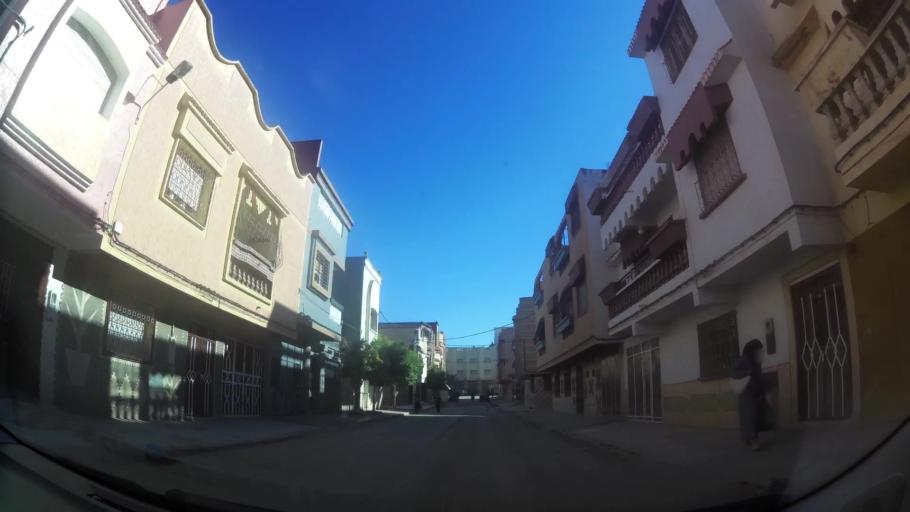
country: MA
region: Oriental
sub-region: Berkane-Taourirt
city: Ahfir
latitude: 34.9572
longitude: -2.1034
